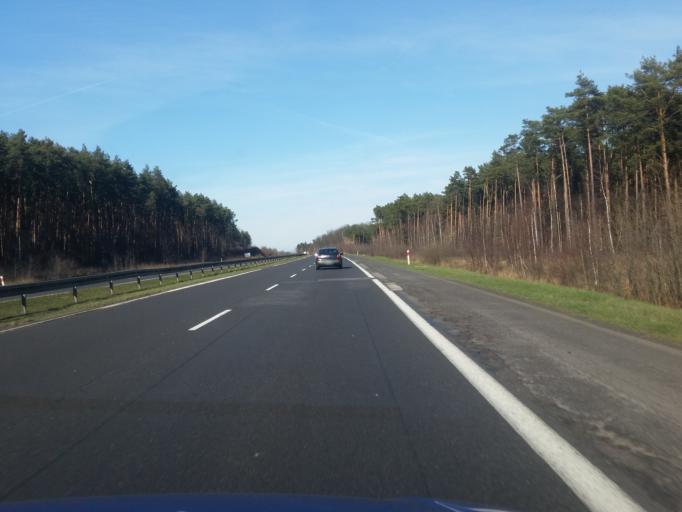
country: PL
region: Lodz Voivodeship
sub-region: Powiat radomszczanski
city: Gomunice
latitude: 51.1632
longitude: 19.4552
